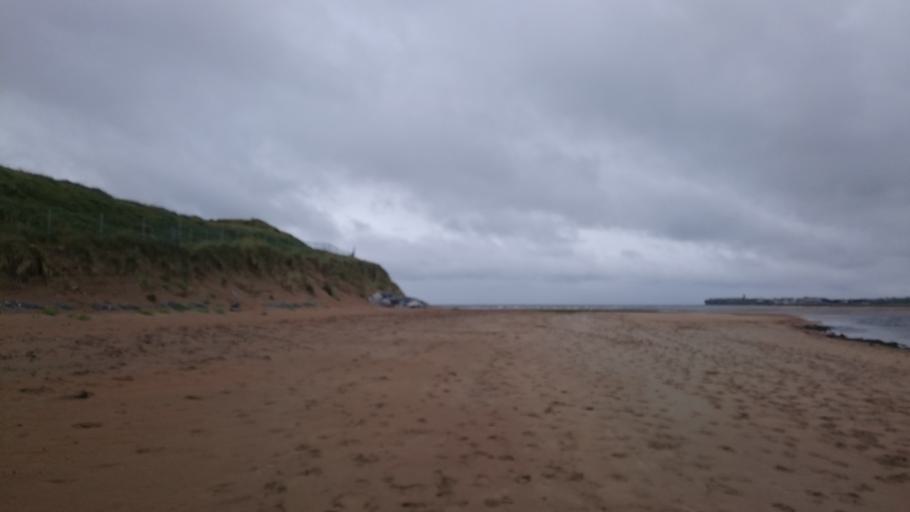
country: IE
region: Munster
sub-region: An Clar
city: Kilrush
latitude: 52.9436
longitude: -9.3569
